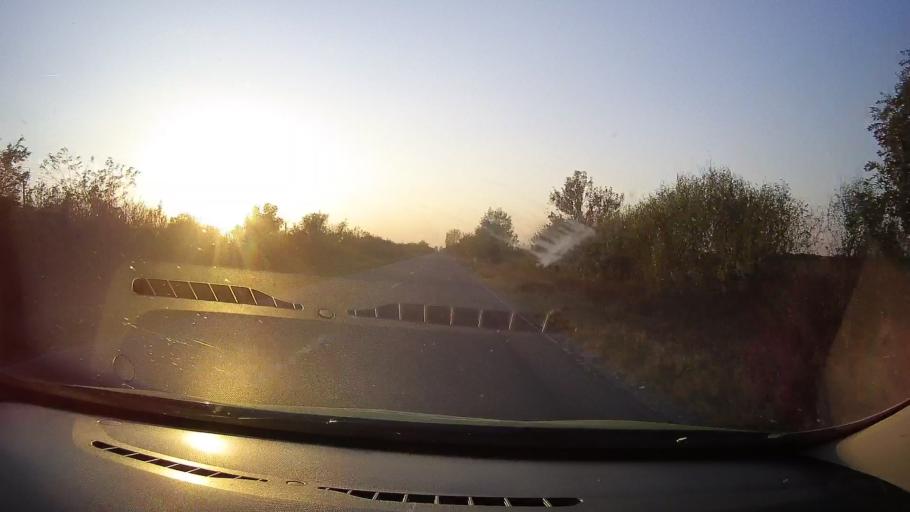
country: RO
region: Arad
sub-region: Comuna Ineu
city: Ineu
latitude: 46.4313
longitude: 21.8130
